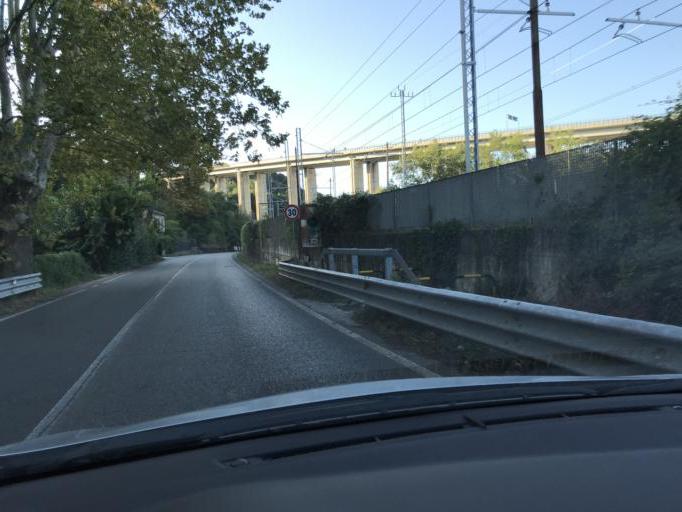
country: IT
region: Latium
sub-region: Provincia di Viterbo
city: Orte
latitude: 42.4493
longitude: 12.3902
